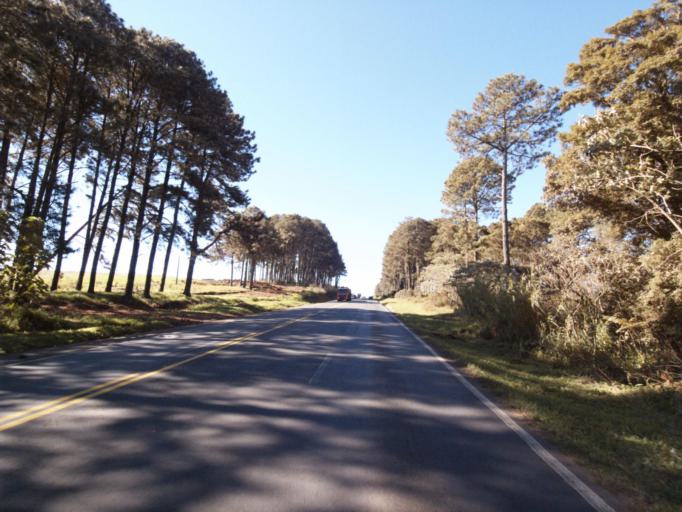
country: BR
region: Santa Catarina
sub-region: Xanxere
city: Xanxere
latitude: -26.9097
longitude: -52.4705
